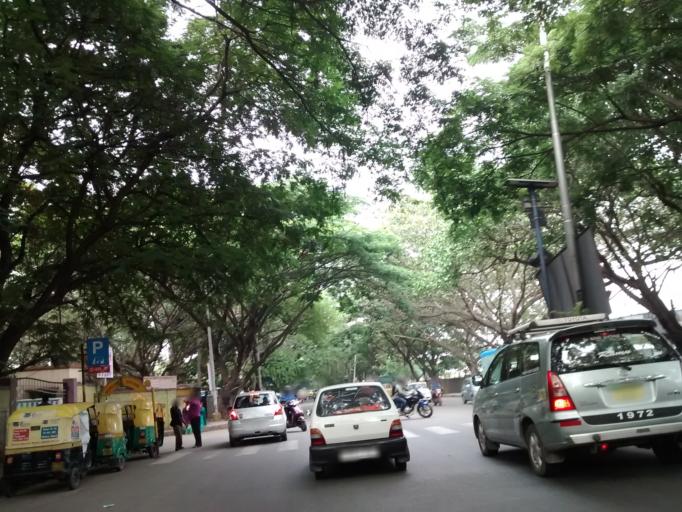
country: IN
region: Karnataka
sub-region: Bangalore Urban
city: Bangalore
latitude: 12.9546
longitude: 77.6821
